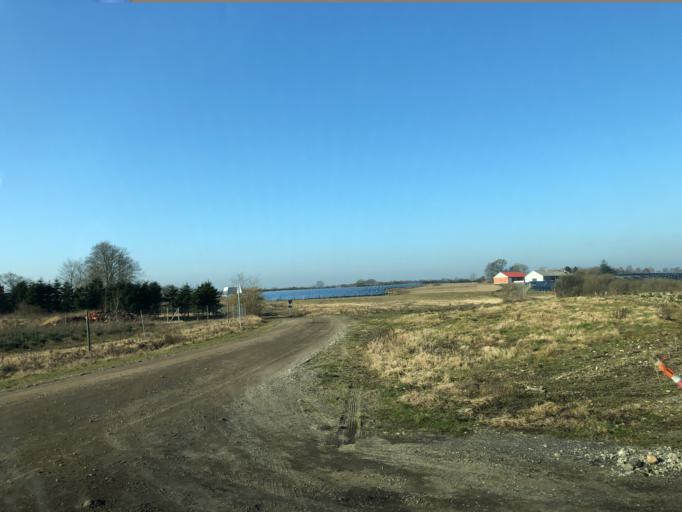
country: DK
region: Central Jutland
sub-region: Silkeborg Kommune
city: Silkeborg
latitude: 56.2048
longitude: 9.5539
